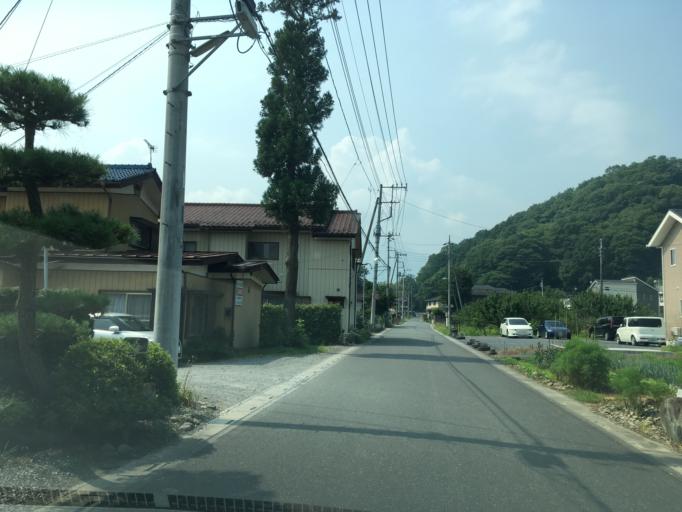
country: JP
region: Saitama
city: Chichibu
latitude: 36.0106
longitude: 139.1088
